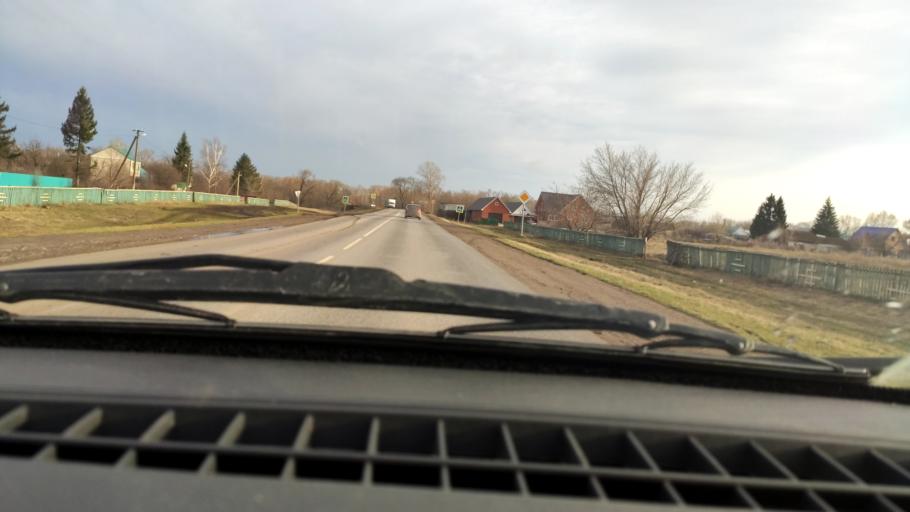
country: RU
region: Bashkortostan
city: Davlekanovo
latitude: 54.3687
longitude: 55.1952
